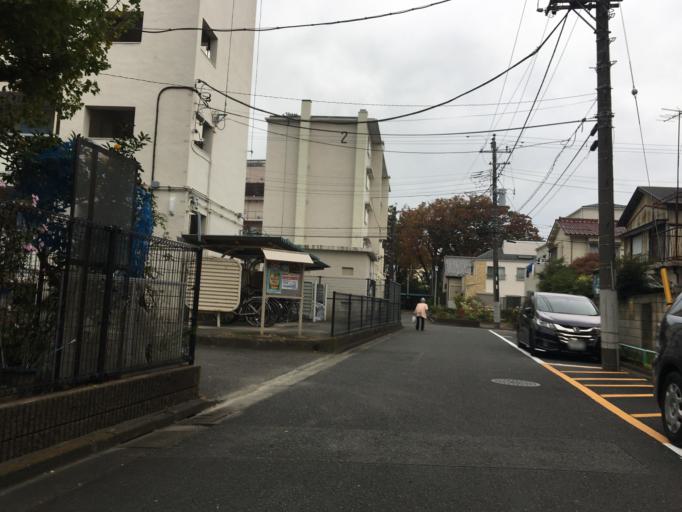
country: JP
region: Tokyo
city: Urayasu
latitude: 35.6781
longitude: 139.8849
